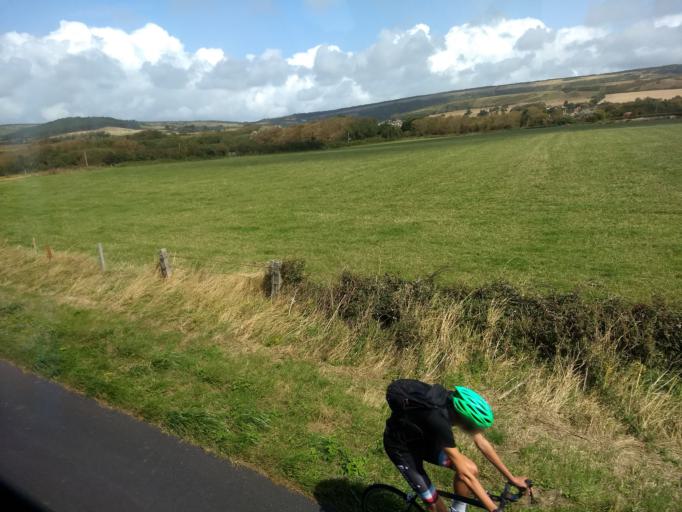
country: GB
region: England
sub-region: Isle of Wight
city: Shalfleet
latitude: 50.6358
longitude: -1.4019
